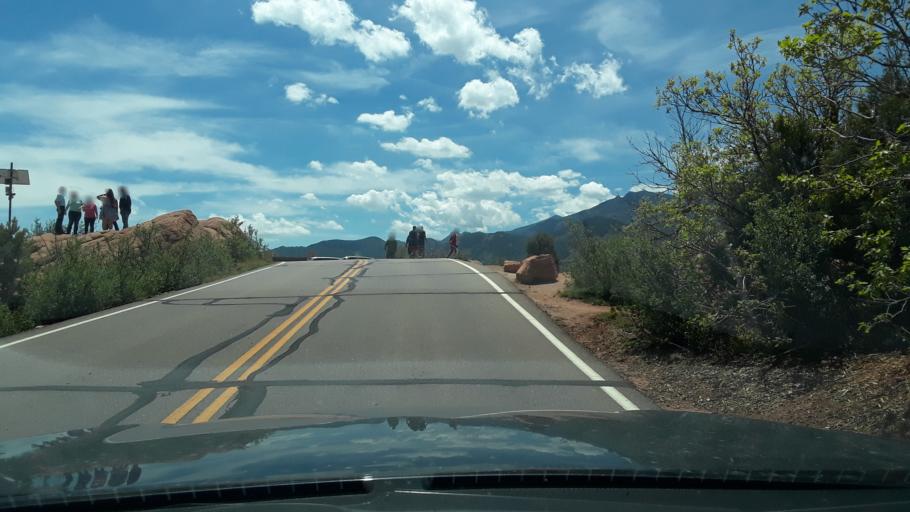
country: US
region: Colorado
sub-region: El Paso County
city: Manitou Springs
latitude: 38.8664
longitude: -104.8791
